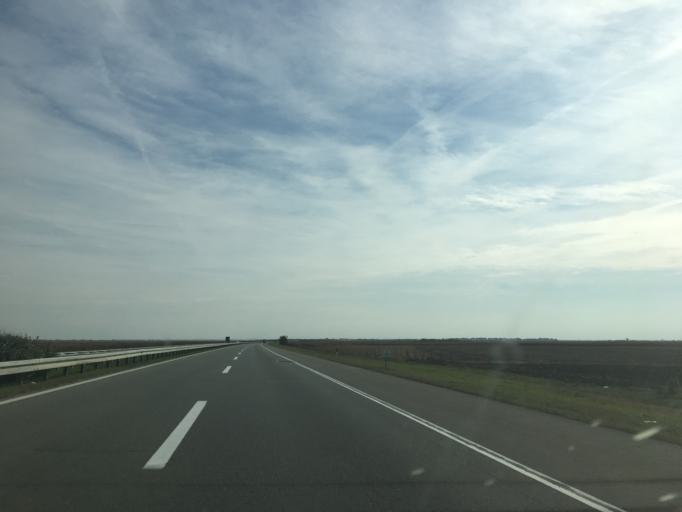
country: RS
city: Novi Karlovci
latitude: 45.0610
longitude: 20.1628
